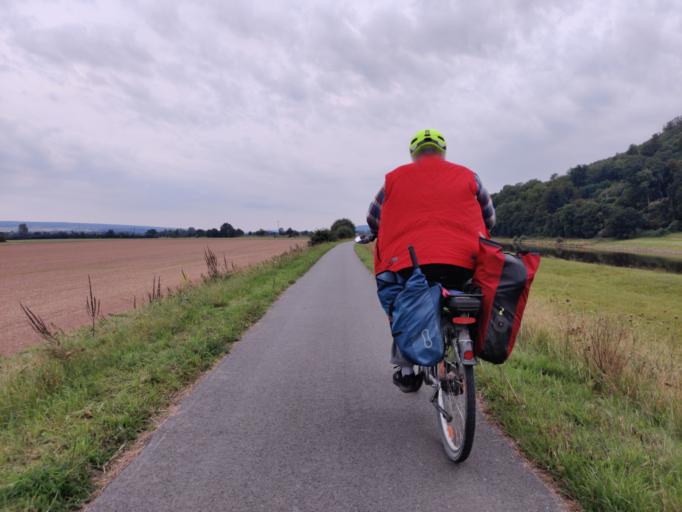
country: DE
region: Lower Saxony
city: Bevern
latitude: 51.8675
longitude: 9.4650
